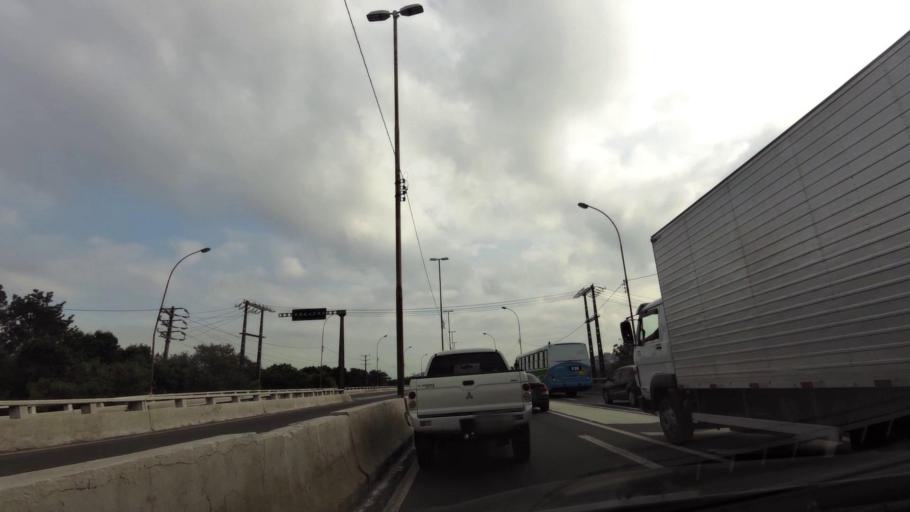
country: BR
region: Espirito Santo
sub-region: Vitoria
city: Vitoria
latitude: -20.3291
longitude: -40.3548
